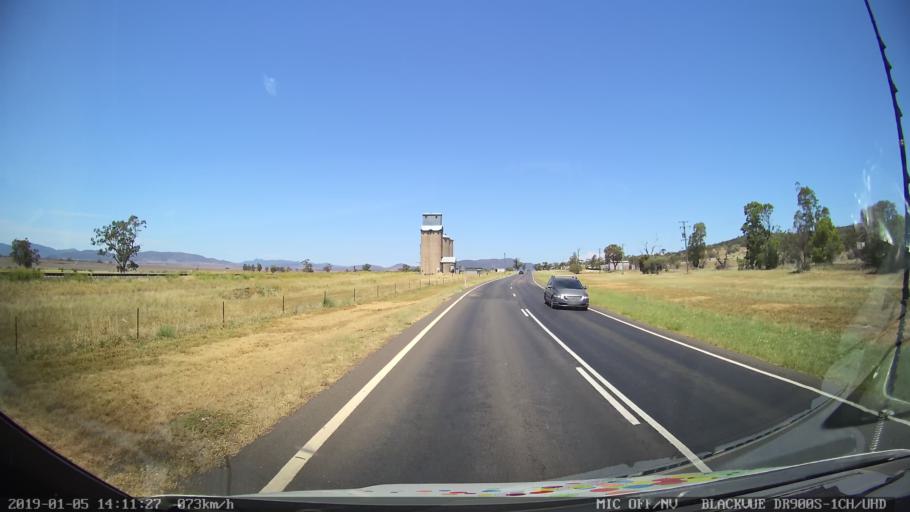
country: AU
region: New South Wales
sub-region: Gunnedah
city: Gunnedah
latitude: -31.2441
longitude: 150.4580
